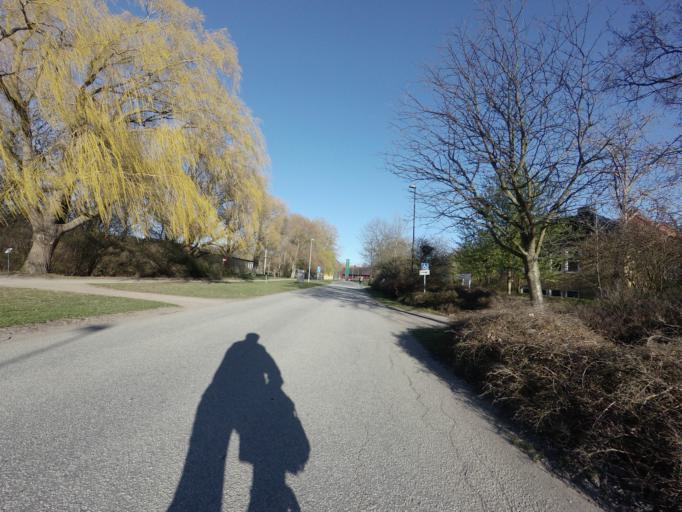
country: SE
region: Skane
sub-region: Lomma Kommun
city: Lomma
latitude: 55.6579
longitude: 13.0802
